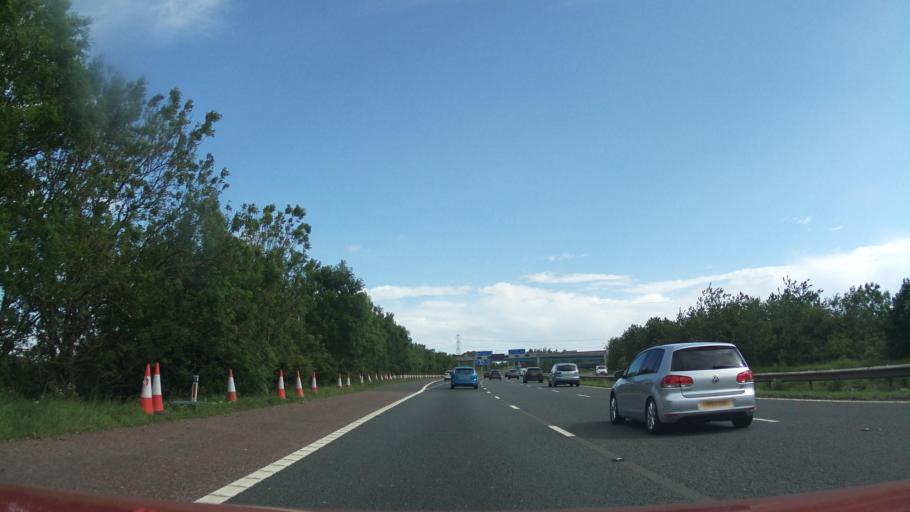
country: GB
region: England
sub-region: Lancashire
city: Clayton-le-Woods
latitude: 53.7235
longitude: -2.6325
